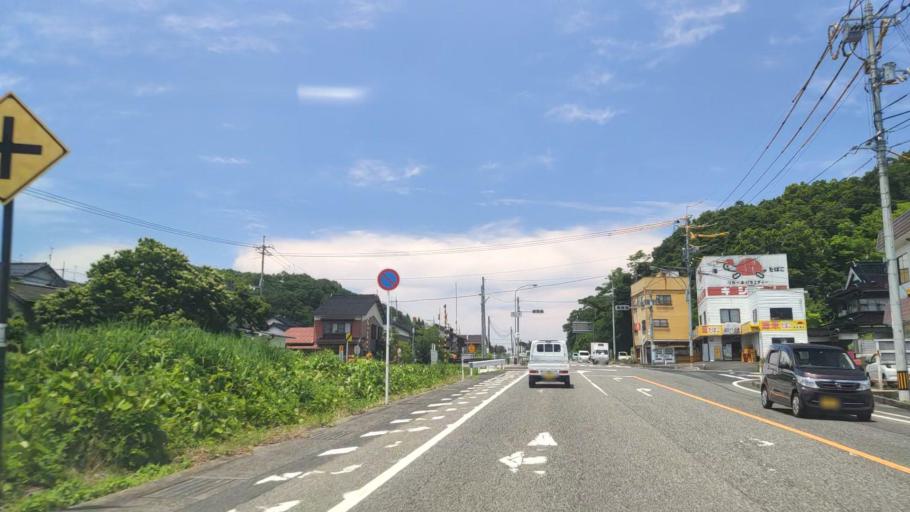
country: JP
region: Tottori
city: Tottori
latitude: 35.4271
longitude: 134.2610
